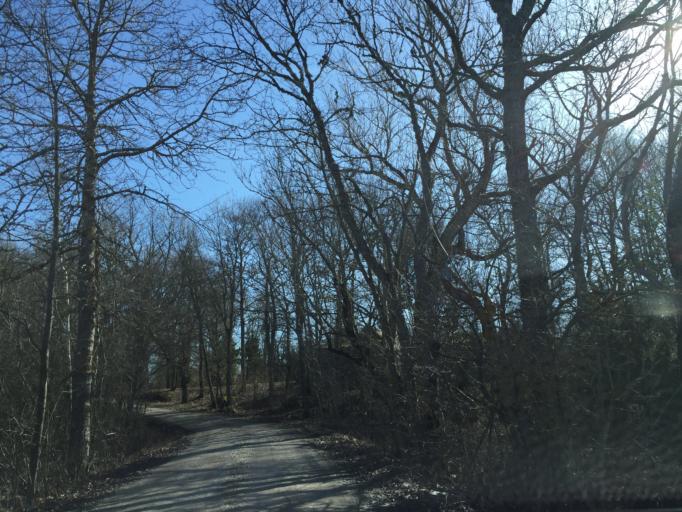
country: EE
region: Laeaene
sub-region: Haapsalu linn
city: Haapsalu
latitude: 58.6827
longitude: 23.5241
